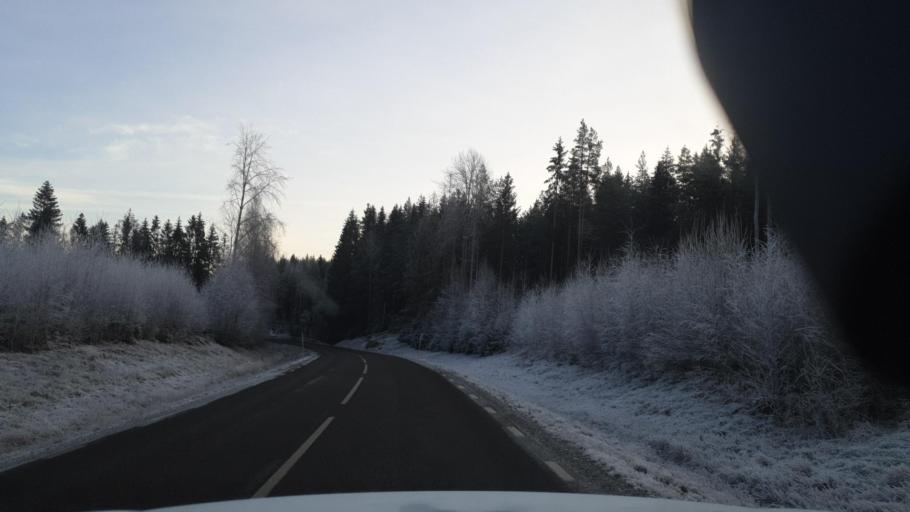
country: SE
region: Vaermland
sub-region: Eda Kommun
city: Amotfors
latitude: 59.7366
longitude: 12.3876
